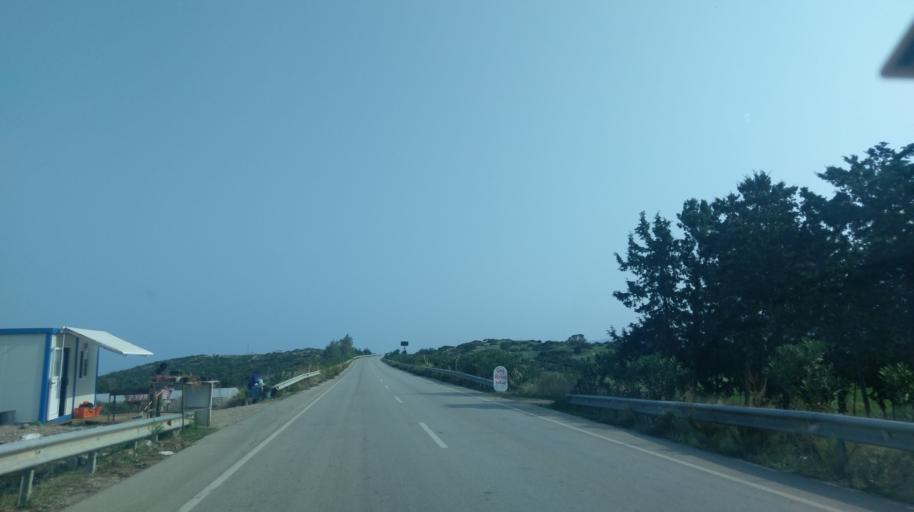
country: CY
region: Ammochostos
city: Lefkonoiko
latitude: 35.4068
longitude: 33.7789
